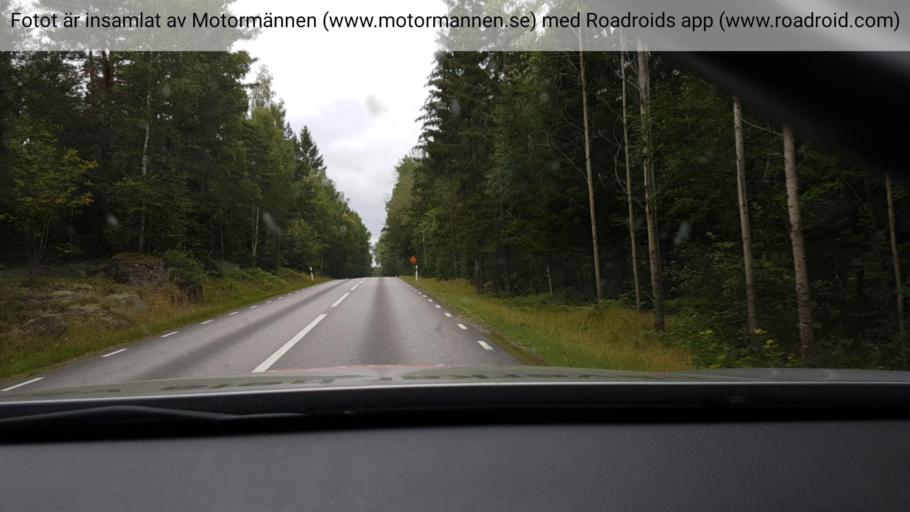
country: SE
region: Stockholm
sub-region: Norrtalje Kommun
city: Skanninge
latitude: 59.8844
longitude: 18.4879
